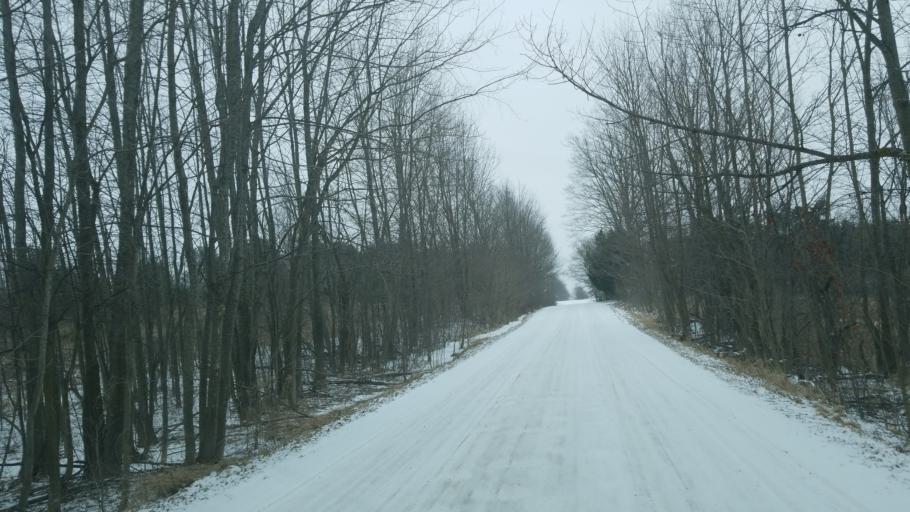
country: US
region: Michigan
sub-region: Osceola County
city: Evart
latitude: 44.0159
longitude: -85.2299
